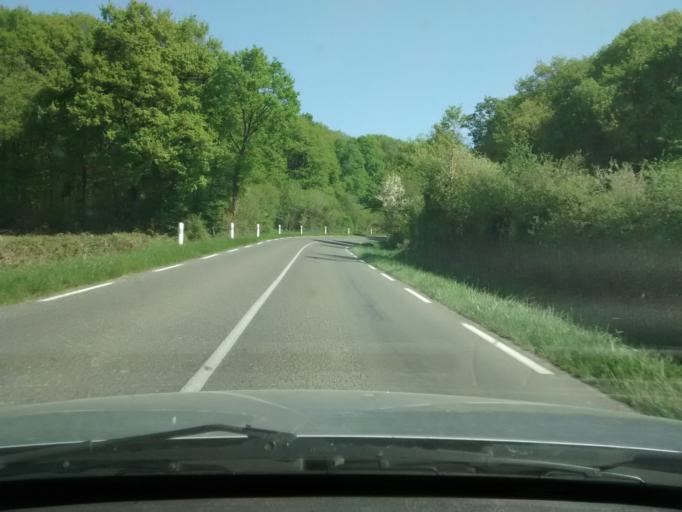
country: FR
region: Pays de la Loire
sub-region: Departement de la Mayenne
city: Montsurs
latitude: 48.1032
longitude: -0.5045
